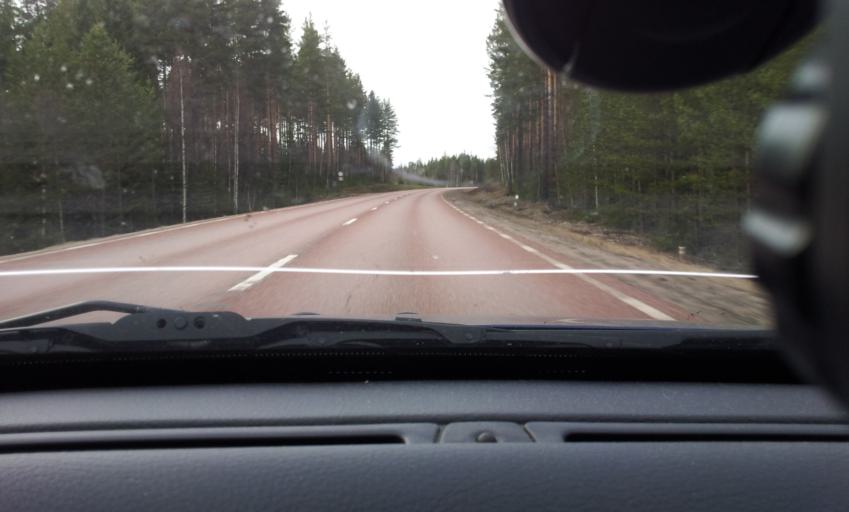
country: SE
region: Gaevleborg
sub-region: Ljusdals Kommun
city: Farila
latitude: 61.8182
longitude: 15.7594
